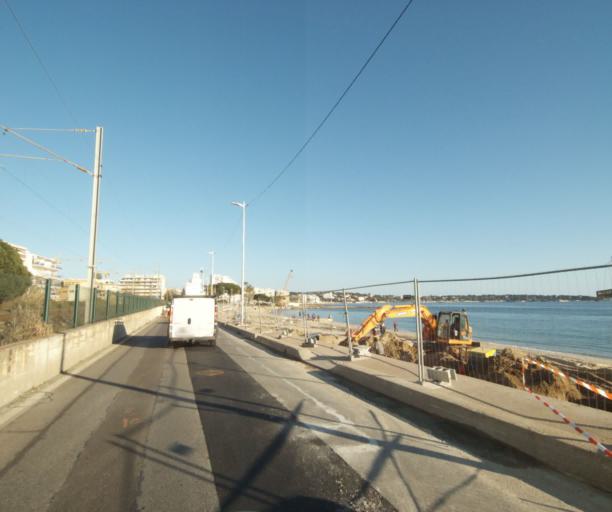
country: FR
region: Provence-Alpes-Cote d'Azur
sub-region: Departement des Alpes-Maritimes
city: Antibes
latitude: 43.5713
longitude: 7.0987
